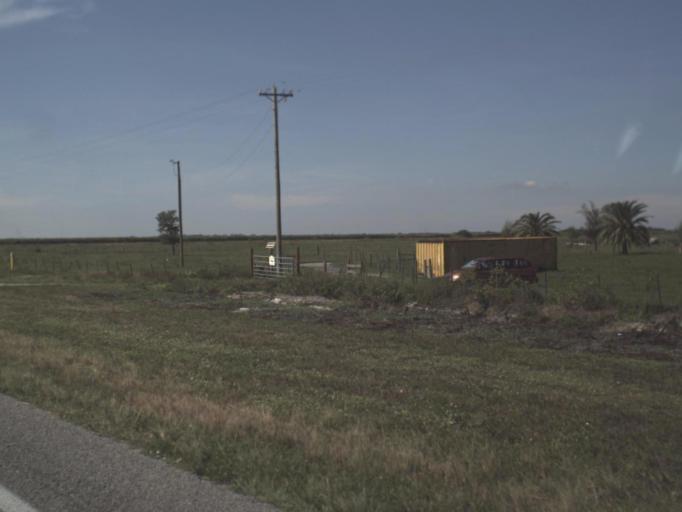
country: US
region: Florida
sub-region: Glades County
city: Moore Haven
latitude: 26.8339
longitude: -81.1601
